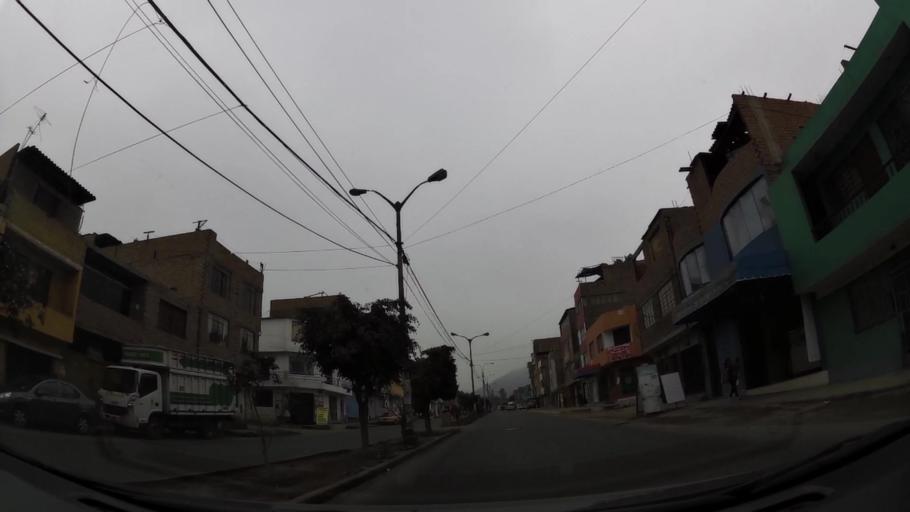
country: PE
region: Lima
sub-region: Lima
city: Urb. Santo Domingo
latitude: -11.9150
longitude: -77.0337
